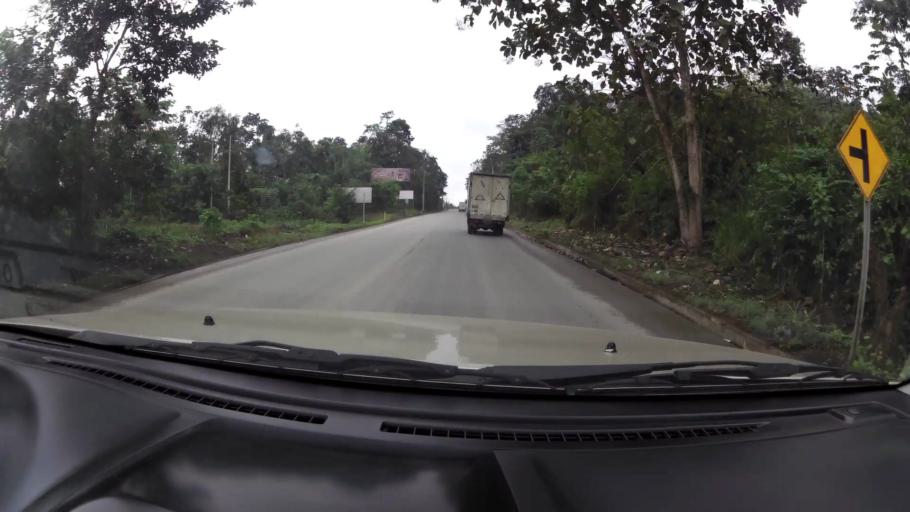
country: EC
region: El Oro
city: Pasaje
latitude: -3.3291
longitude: -79.7628
